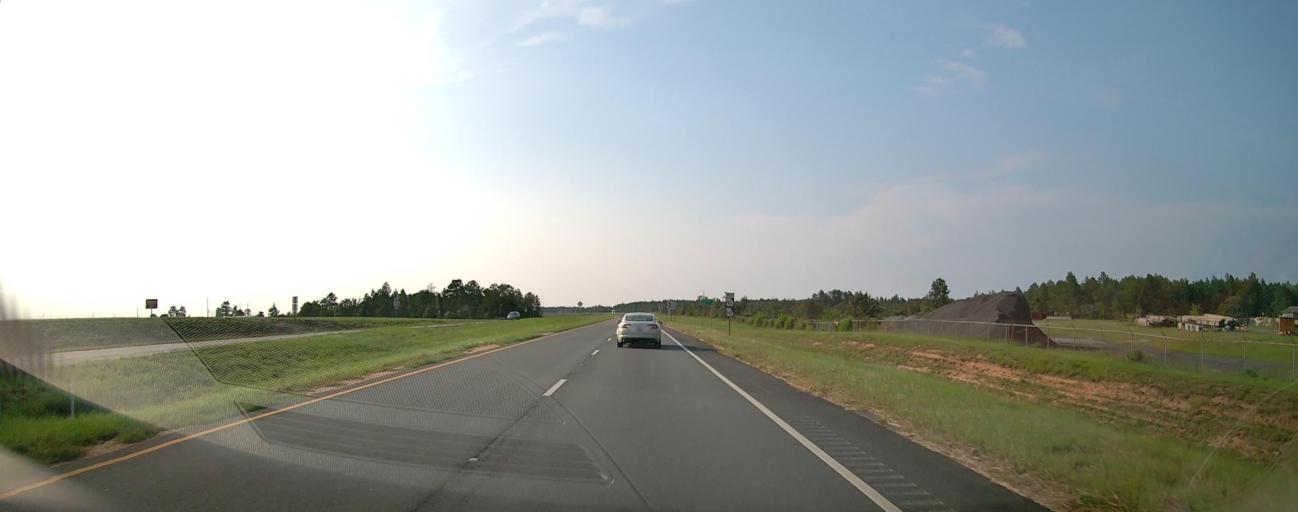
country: US
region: Georgia
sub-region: Taylor County
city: Butler
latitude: 32.5541
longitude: -84.2638
